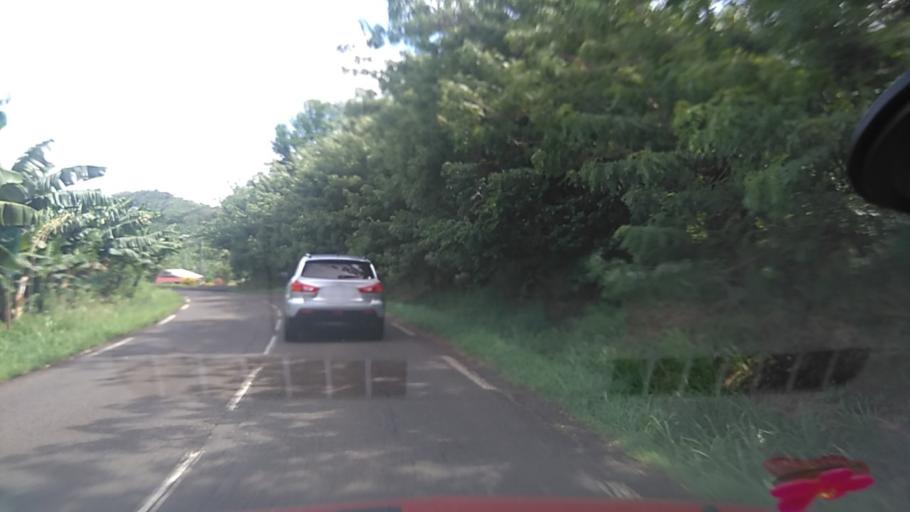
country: MQ
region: Martinique
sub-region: Martinique
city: Saint-Esprit
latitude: 14.5825
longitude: -60.9252
